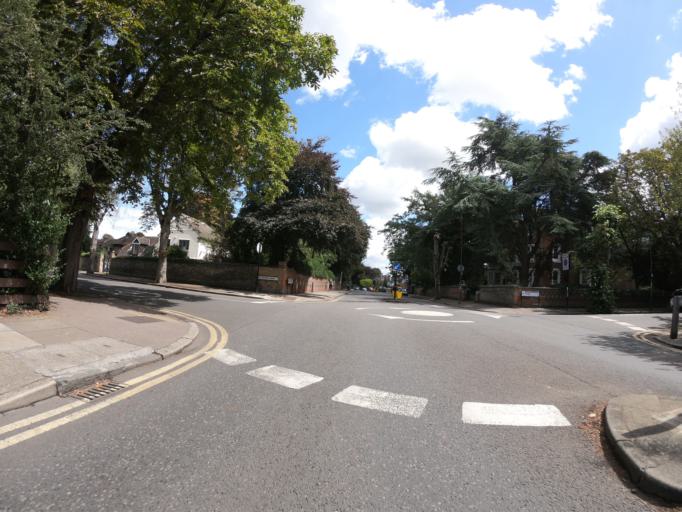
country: GB
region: England
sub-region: Greater London
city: Blackheath
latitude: 51.4788
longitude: 0.0139
